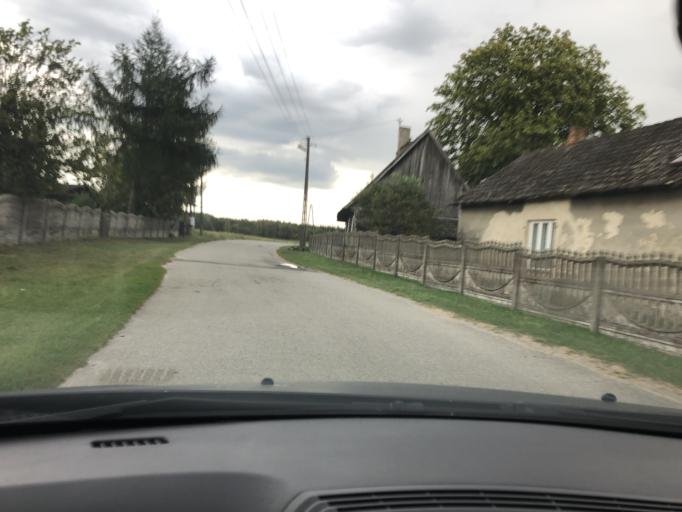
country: PL
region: Lodz Voivodeship
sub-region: Powiat wieruszowski
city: Czastary
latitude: 51.2426
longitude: 18.2771
